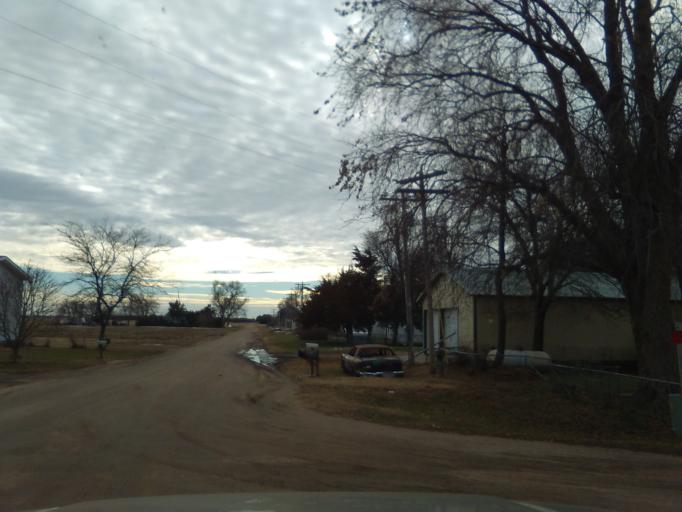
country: US
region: Nebraska
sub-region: Buffalo County
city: Gibbon
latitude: 40.6476
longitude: -98.8473
